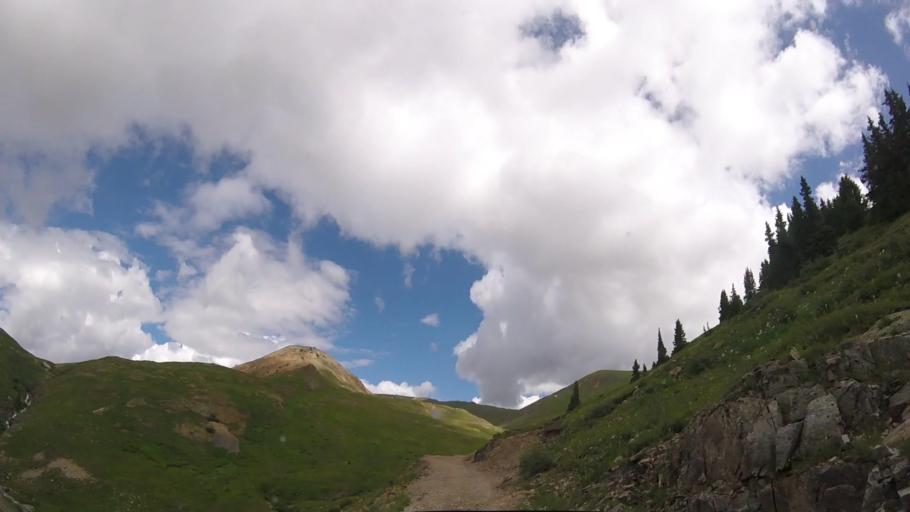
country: US
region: Colorado
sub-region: Ouray County
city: Ouray
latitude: 37.9453
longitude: -107.5741
